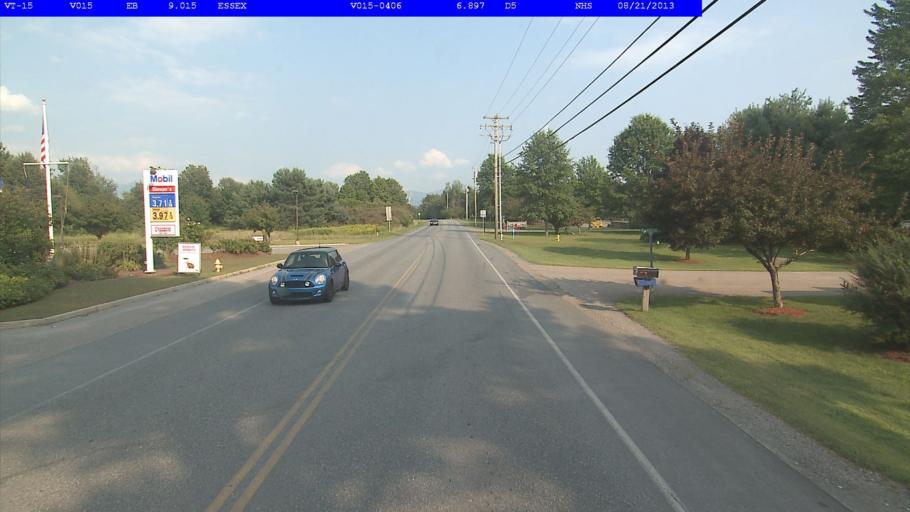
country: US
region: Vermont
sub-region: Chittenden County
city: Jericho
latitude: 44.5027
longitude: -73.0316
